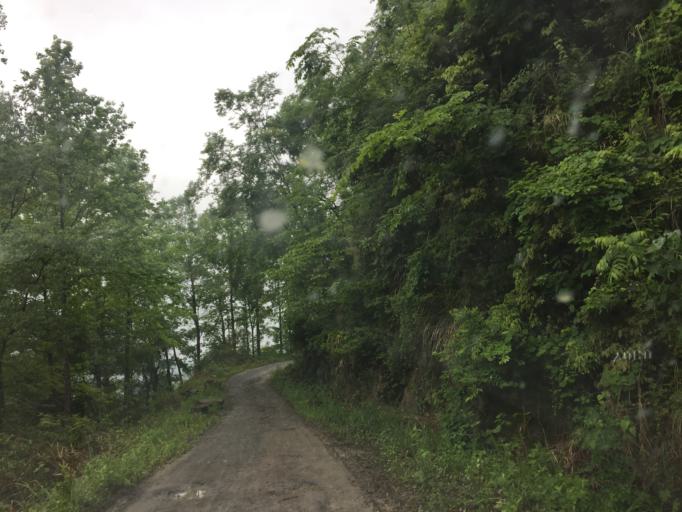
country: CN
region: Guizhou Sheng
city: Donghua
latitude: 28.0609
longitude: 108.1016
